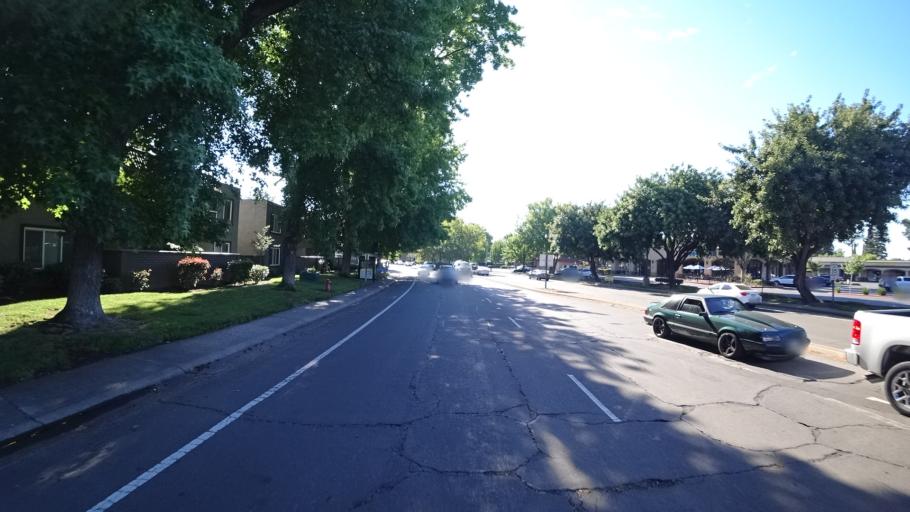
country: US
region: California
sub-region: Sacramento County
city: Rosemont
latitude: 38.5641
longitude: -121.3804
